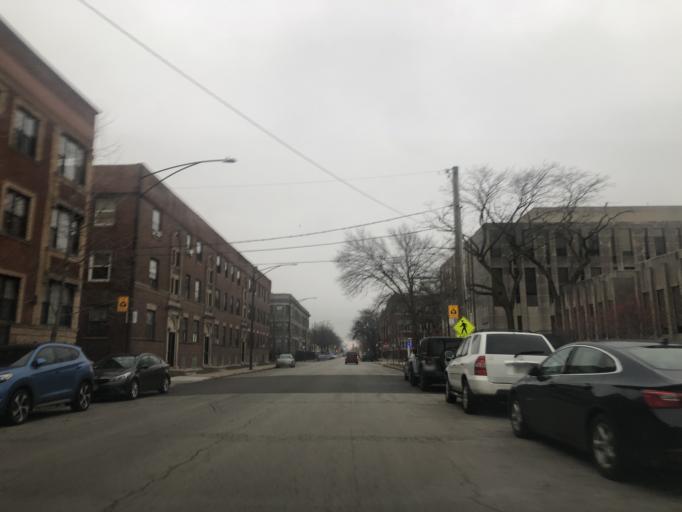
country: US
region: Illinois
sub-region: Cook County
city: Chicago
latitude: 41.7841
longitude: -87.6015
